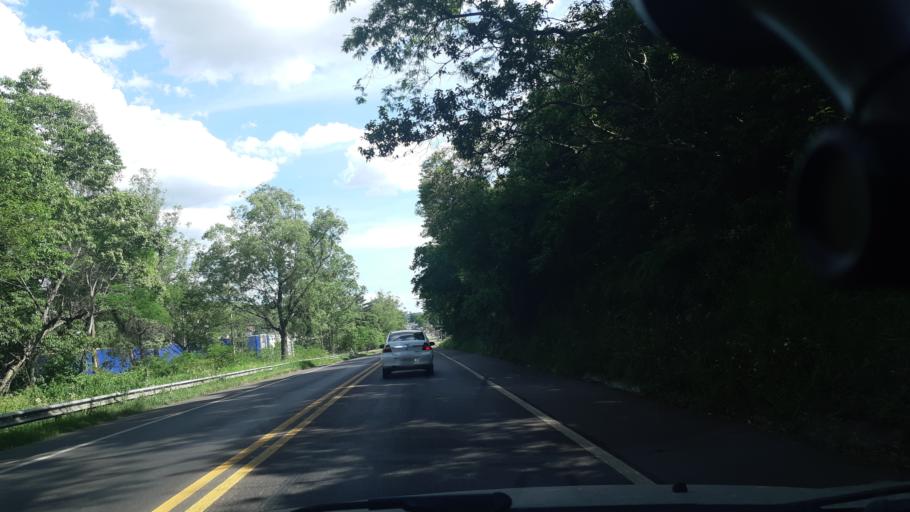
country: BR
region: Rio Grande do Sul
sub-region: Estancia Velha
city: Estancia Velha
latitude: -29.6427
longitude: -51.1428
